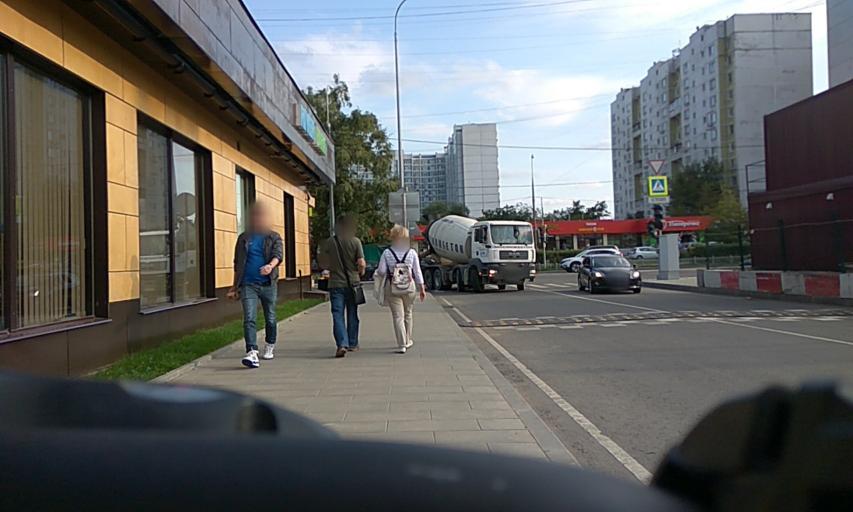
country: RU
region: Moscow
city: Kolomenskoye
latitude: 55.6791
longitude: 37.6958
